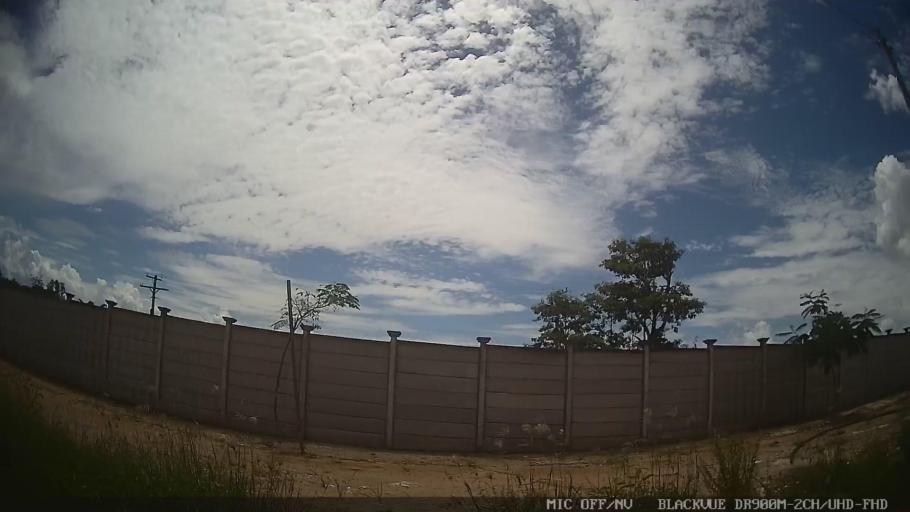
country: BR
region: Sao Paulo
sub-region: Conchas
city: Conchas
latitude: -23.0929
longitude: -47.9843
